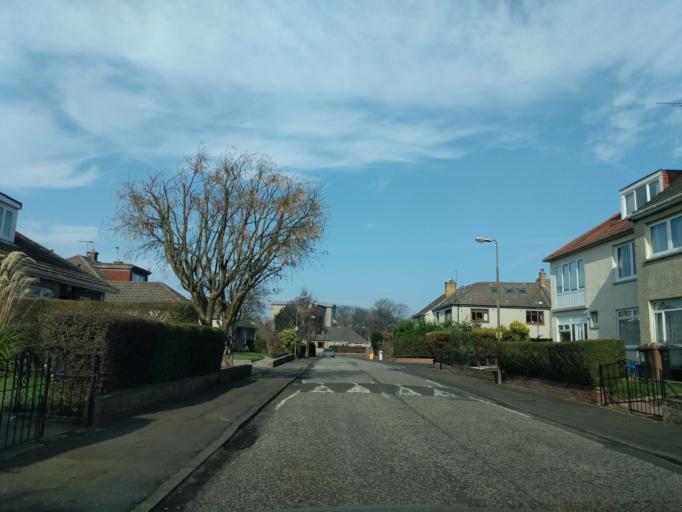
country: GB
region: Scotland
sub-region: Edinburgh
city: Currie
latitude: 55.9504
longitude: -3.2935
